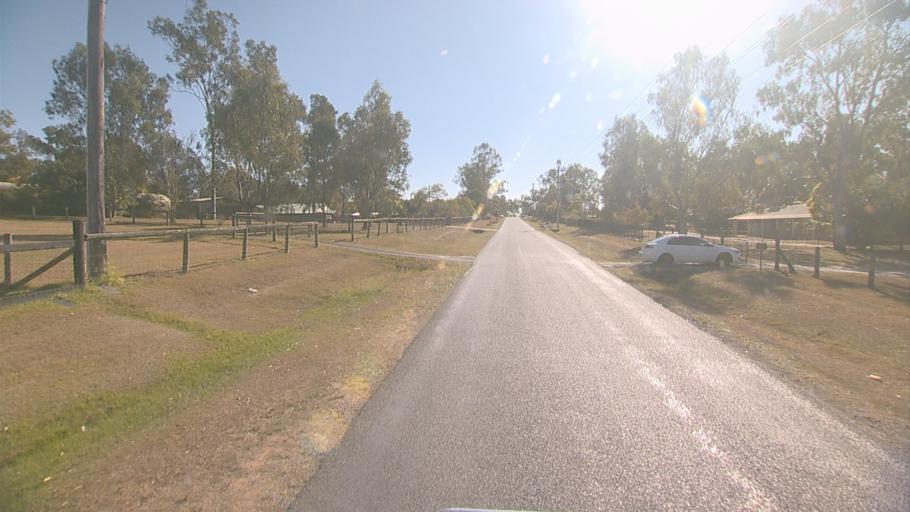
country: AU
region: Queensland
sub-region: Logan
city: Cedar Vale
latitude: -27.8379
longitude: 153.0316
